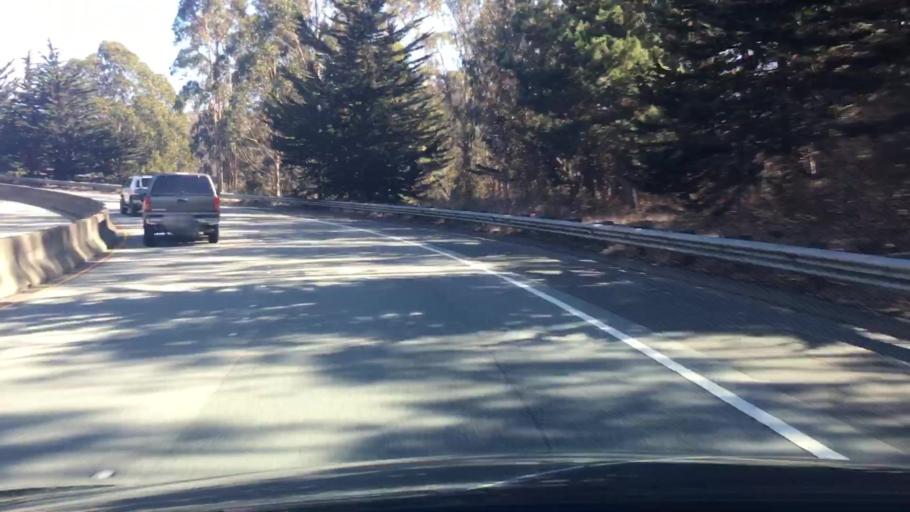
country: US
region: California
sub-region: San Mateo County
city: Pacifica
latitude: 37.6272
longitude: -122.4784
